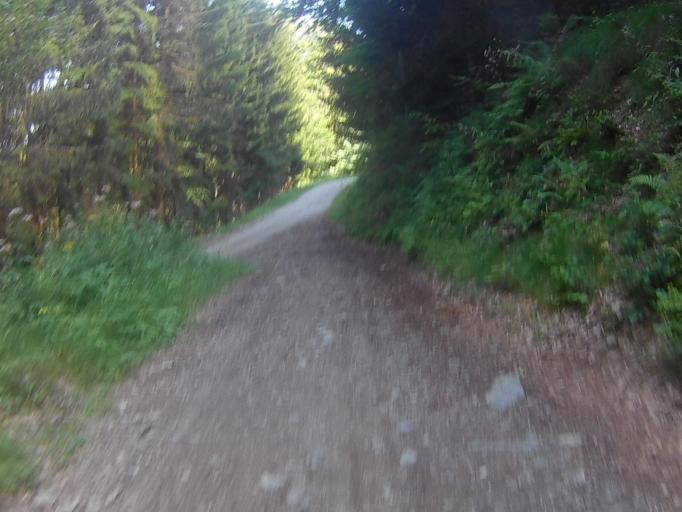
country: SI
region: Ruse
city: Bistrica ob Dravi
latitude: 46.5168
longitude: 15.5554
